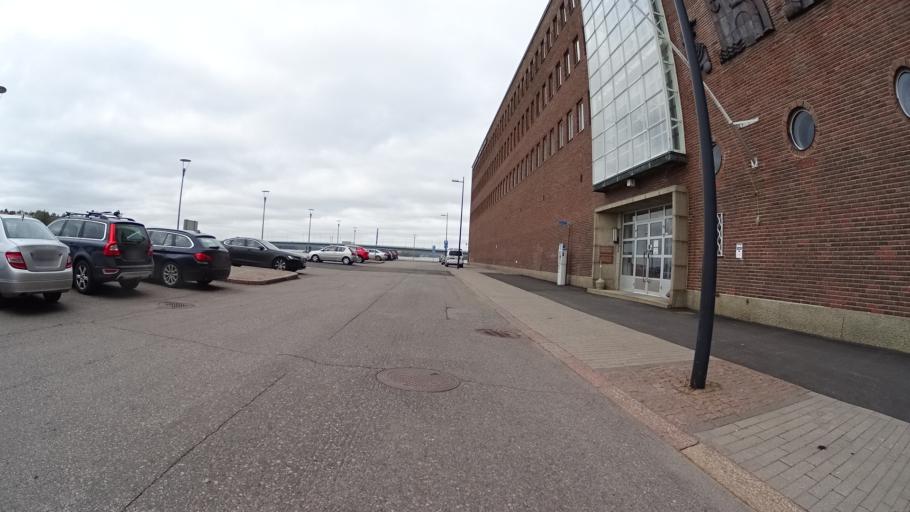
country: FI
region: Uusimaa
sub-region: Helsinki
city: Helsinki
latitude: 60.1631
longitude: 24.9004
